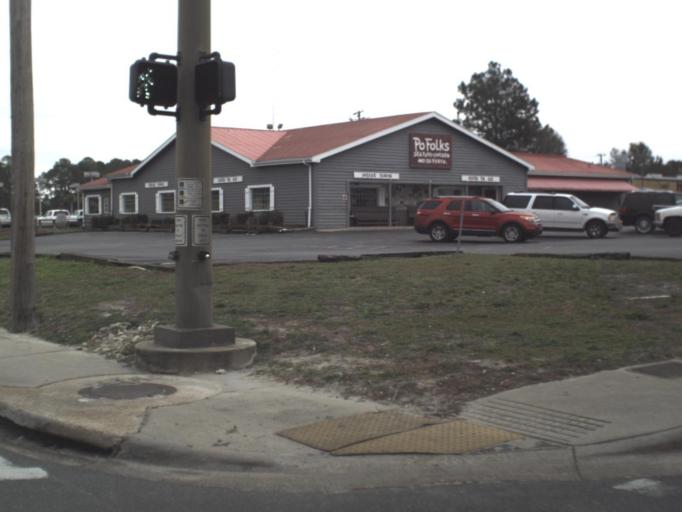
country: US
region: Florida
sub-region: Bay County
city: Panama City
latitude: 30.1752
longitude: -85.6754
